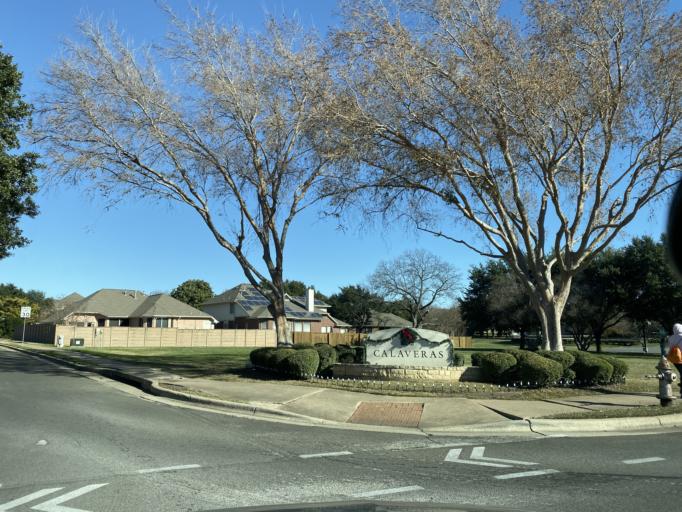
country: US
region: Texas
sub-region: Williamson County
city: Brushy Creek
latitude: 30.4885
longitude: -97.7695
